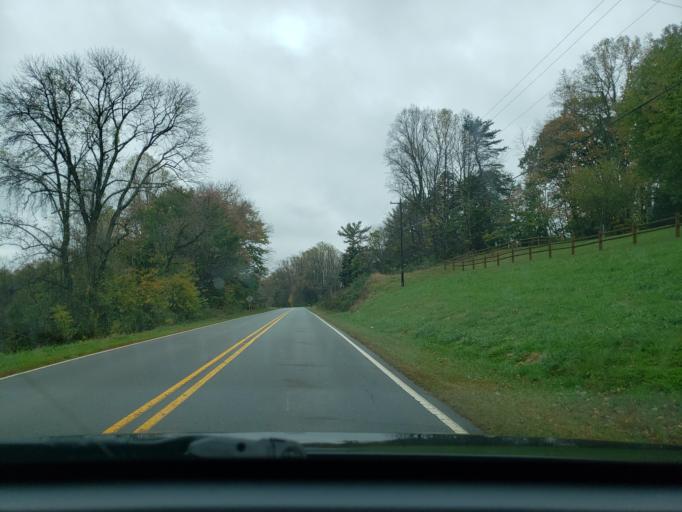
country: US
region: North Carolina
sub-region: Stokes County
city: Walnut Cove
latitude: 36.3501
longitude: -80.1547
